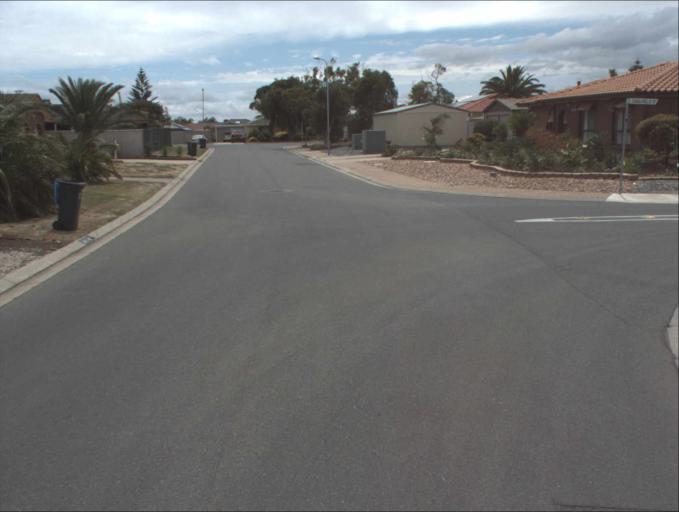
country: AU
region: South Australia
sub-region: Port Adelaide Enfield
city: Birkenhead
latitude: -34.7856
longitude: 138.4959
